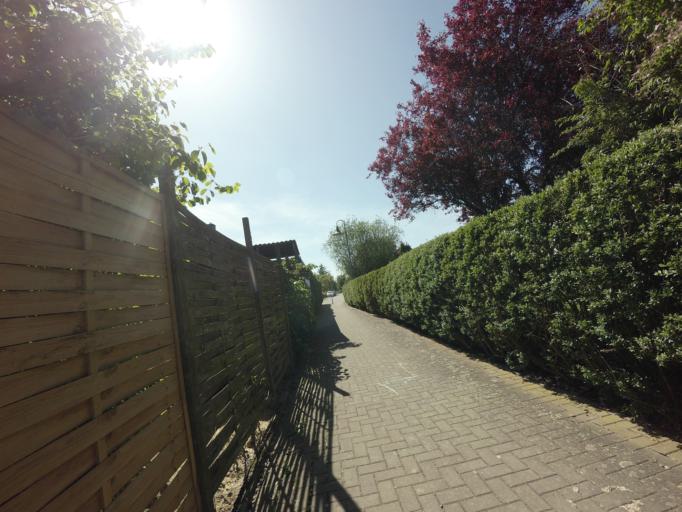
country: DE
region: Lower Saxony
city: Lehre
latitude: 52.2941
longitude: 10.6616
